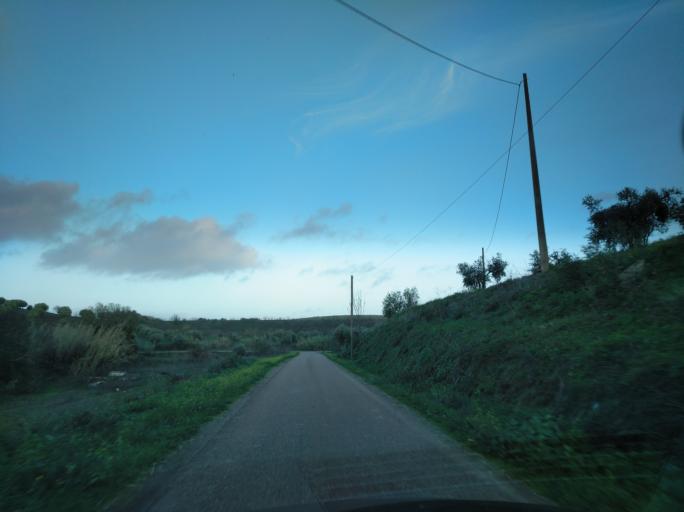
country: PT
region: Portalegre
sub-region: Campo Maior
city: Campo Maior
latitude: 39.0127
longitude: -7.1238
